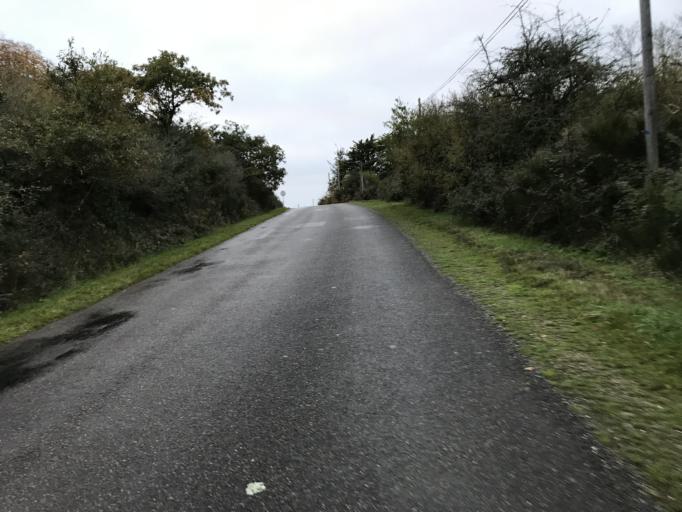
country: FR
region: Brittany
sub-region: Departement du Finistere
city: Logonna-Daoulas
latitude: 48.3186
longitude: -4.3219
